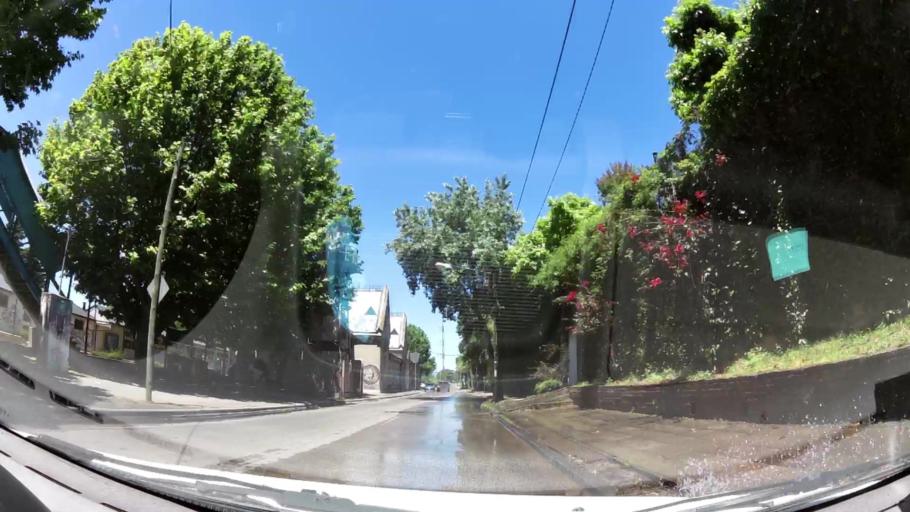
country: AR
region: Buenos Aires
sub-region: Partido de Vicente Lopez
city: Olivos
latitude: -34.4887
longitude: -58.4815
